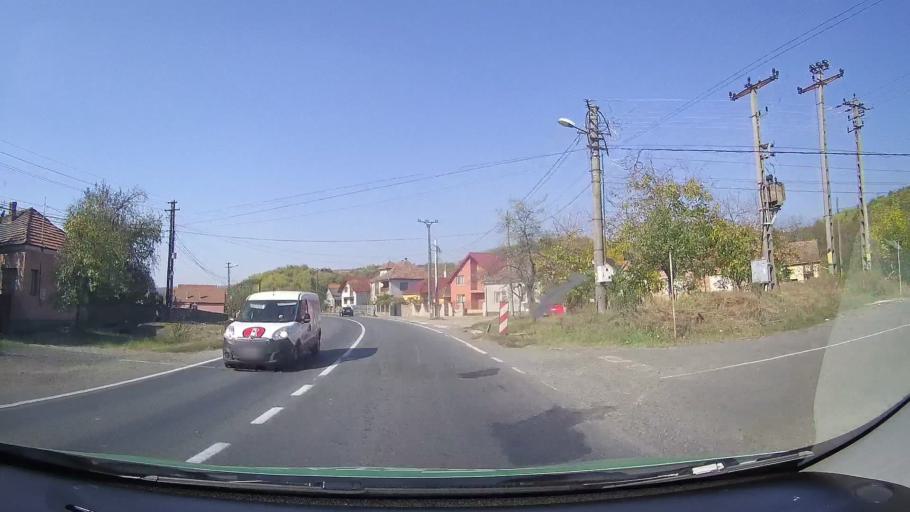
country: RO
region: Arad
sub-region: Oras Lipova
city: Radna
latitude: 46.0961
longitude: 21.6796
